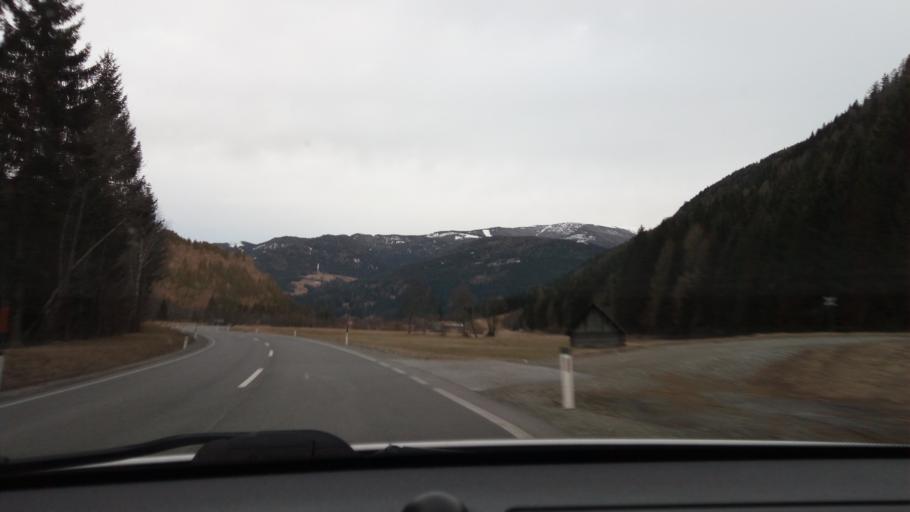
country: AT
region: Styria
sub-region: Politischer Bezirk Murau
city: Stadl an der Mur
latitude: 47.0843
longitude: 13.9455
